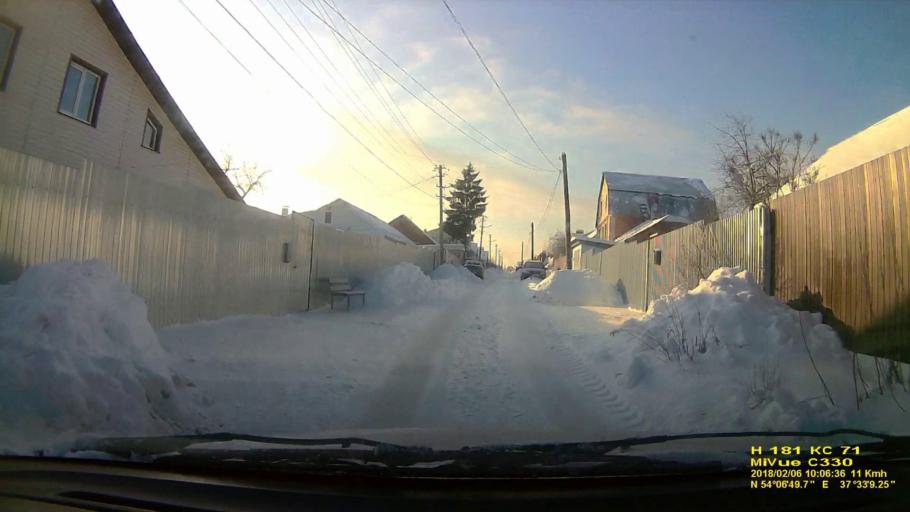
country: RU
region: Tula
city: Kosaya Gora
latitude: 54.1137
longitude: 37.5526
